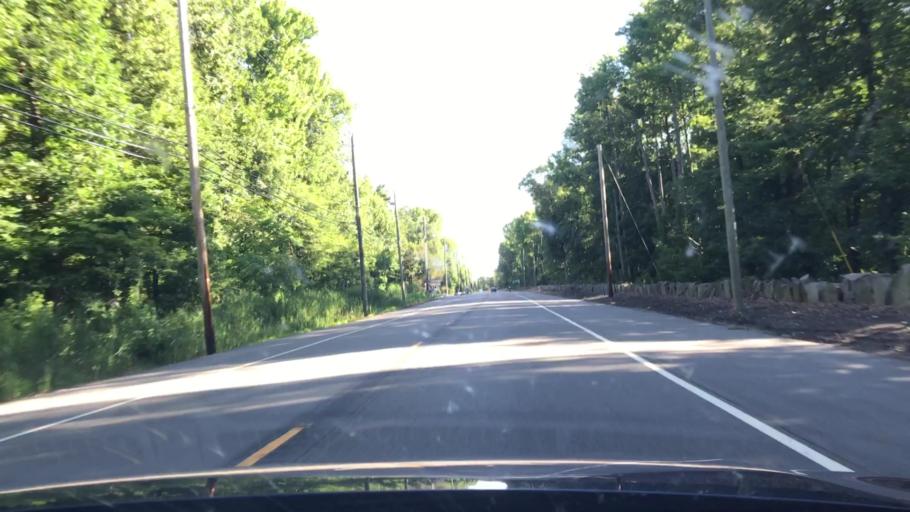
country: US
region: New Jersey
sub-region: Bergen County
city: Alpine
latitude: 40.9723
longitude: -73.9158
